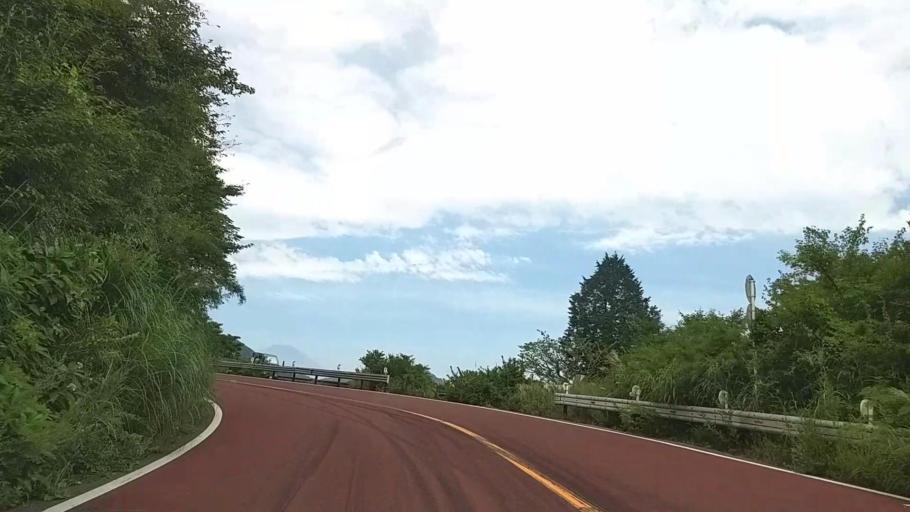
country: JP
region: Kanagawa
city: Hakone
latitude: 35.1885
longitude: 139.0151
